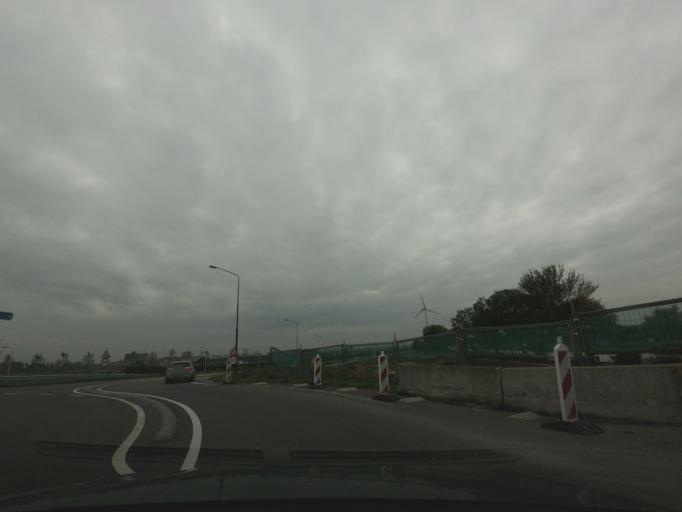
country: NL
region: North Holland
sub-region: Gemeente Langedijk
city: Broek op Langedijk
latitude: 52.6571
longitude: 4.8011
